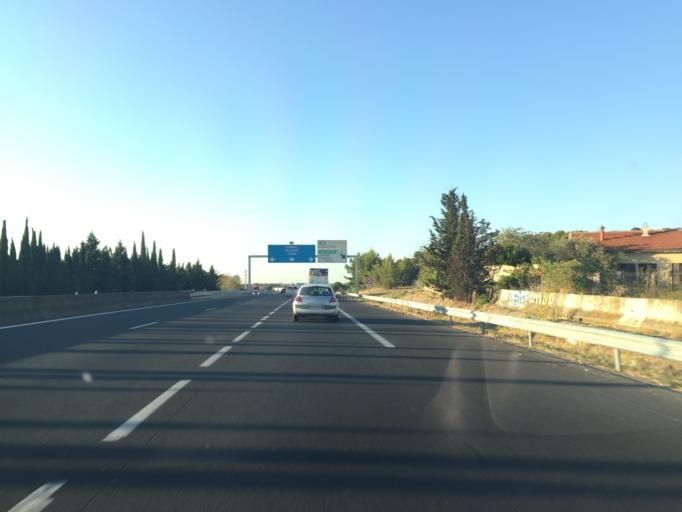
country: FR
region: Provence-Alpes-Cote d'Azur
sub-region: Departement du Vaucluse
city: Vedene
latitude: 43.9746
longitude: 4.8953
